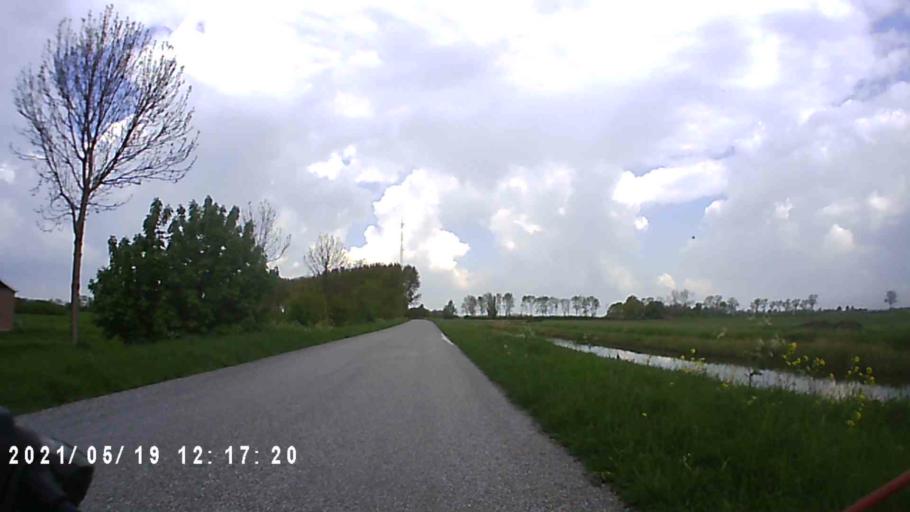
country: NL
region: Friesland
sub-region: Gemeente Kollumerland en Nieuwkruisland
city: Kollum
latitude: 53.2578
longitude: 6.1760
